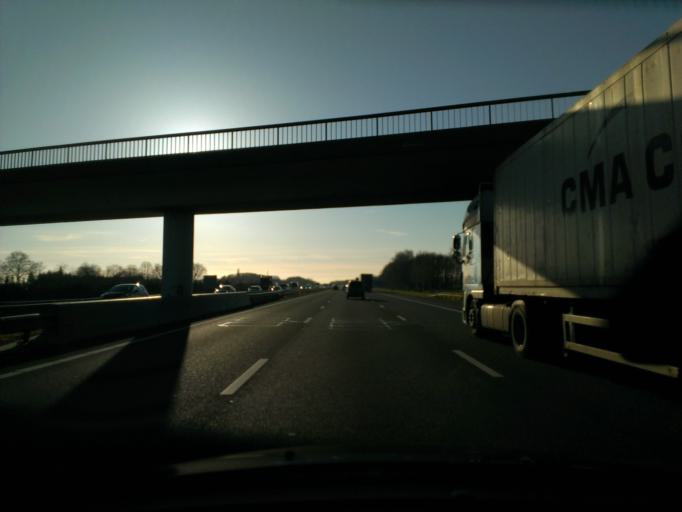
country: NL
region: Gelderland
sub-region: Gemeente Lochem
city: Laren
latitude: 52.2515
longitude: 6.4176
